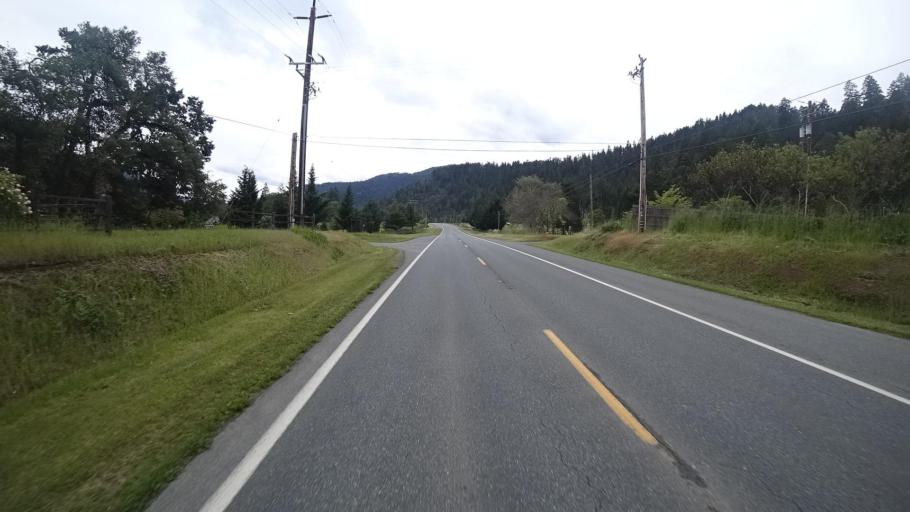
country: US
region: California
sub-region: Humboldt County
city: Willow Creek
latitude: 40.9618
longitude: -123.6424
